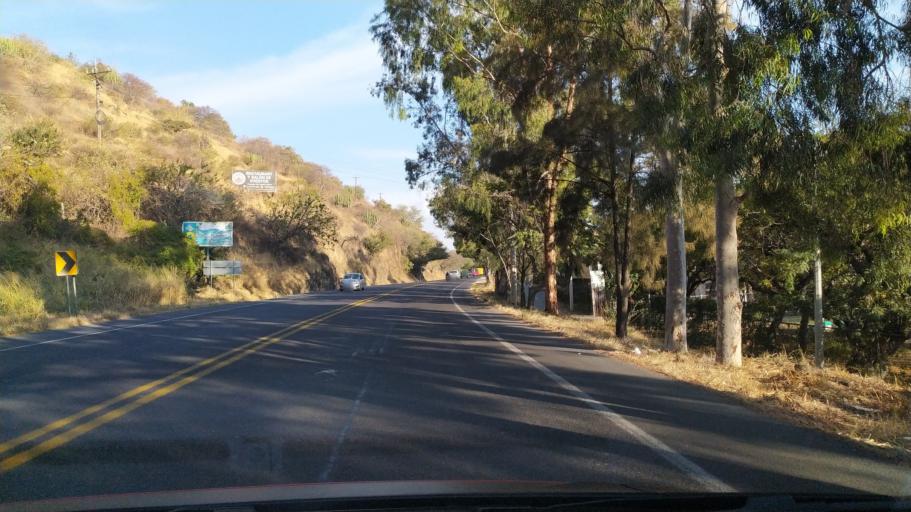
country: MX
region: Jalisco
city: Jamay
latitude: 20.2929
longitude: -102.7265
